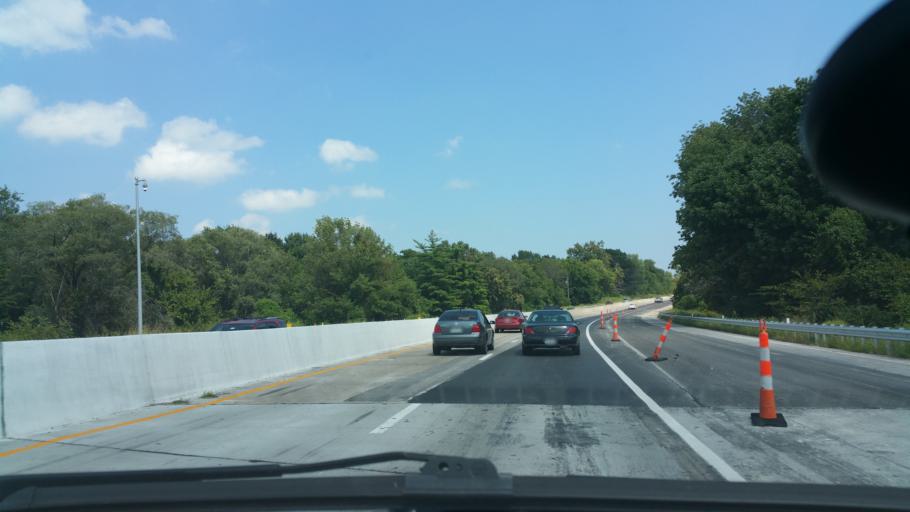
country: US
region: Missouri
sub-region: Clay County
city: Claycomo
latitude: 39.2011
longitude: -94.5062
